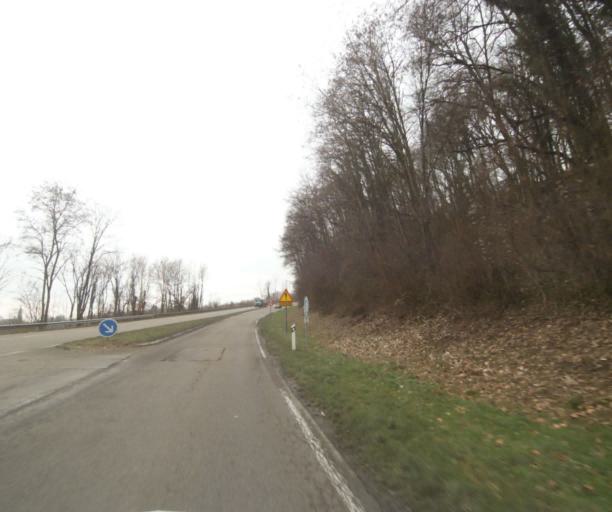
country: FR
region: Champagne-Ardenne
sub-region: Departement de la Haute-Marne
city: Bienville
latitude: 48.5919
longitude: 5.0313
